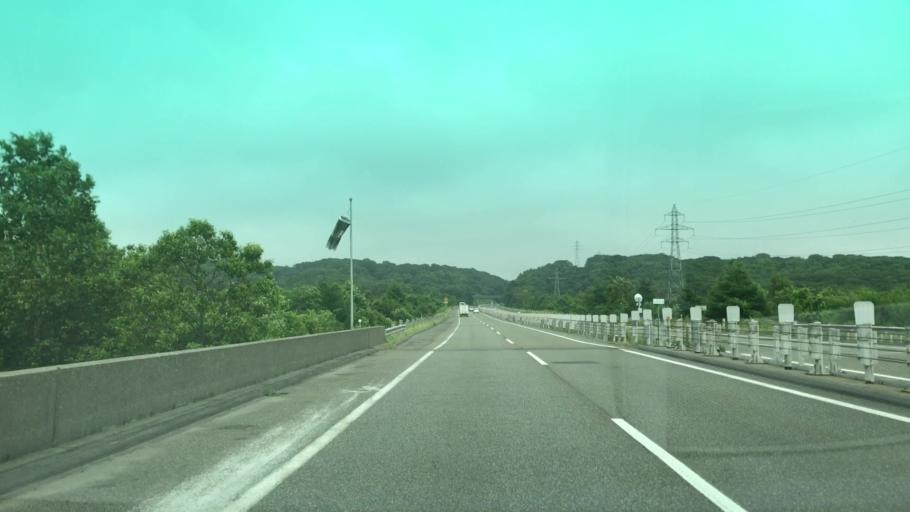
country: JP
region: Hokkaido
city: Tomakomai
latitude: 42.6575
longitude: 141.5746
